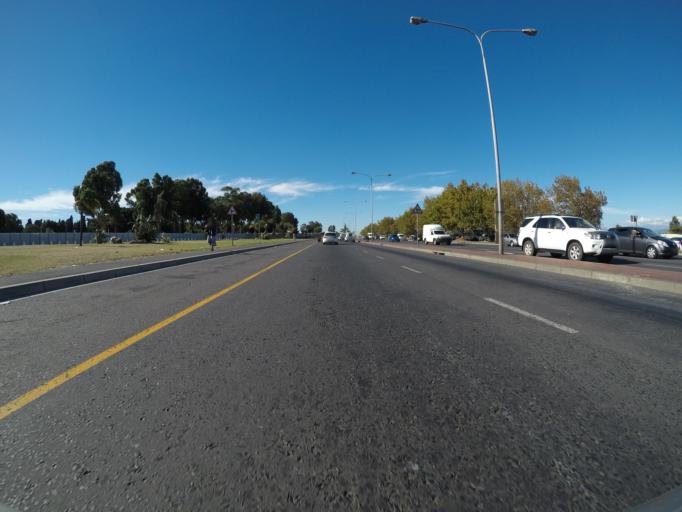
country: ZA
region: Western Cape
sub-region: City of Cape Town
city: Kraaifontein
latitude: -33.9110
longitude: 18.6655
